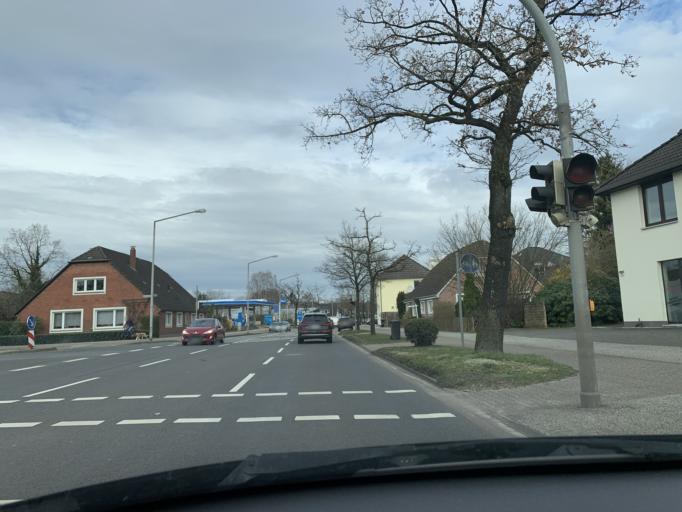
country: DE
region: Lower Saxony
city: Oldenburg
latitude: 53.1249
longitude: 8.1909
